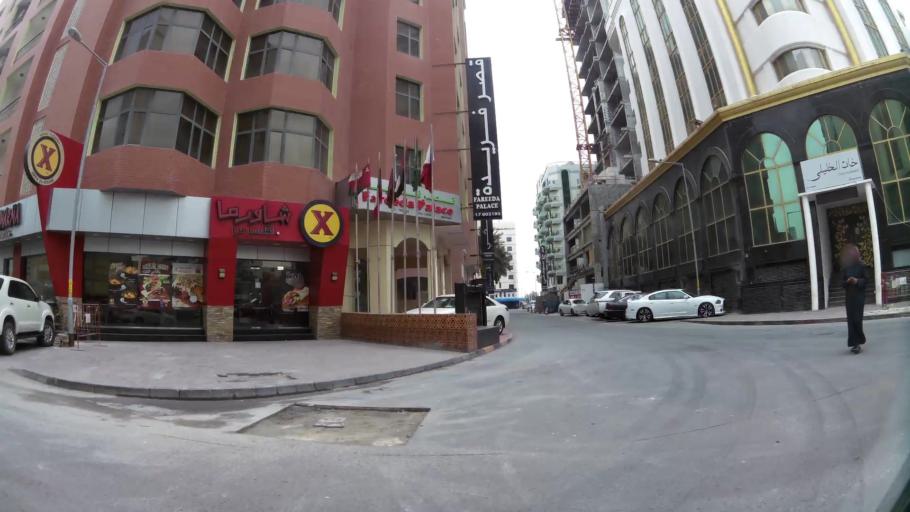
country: BH
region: Manama
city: Manama
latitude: 26.2346
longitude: 50.5957
